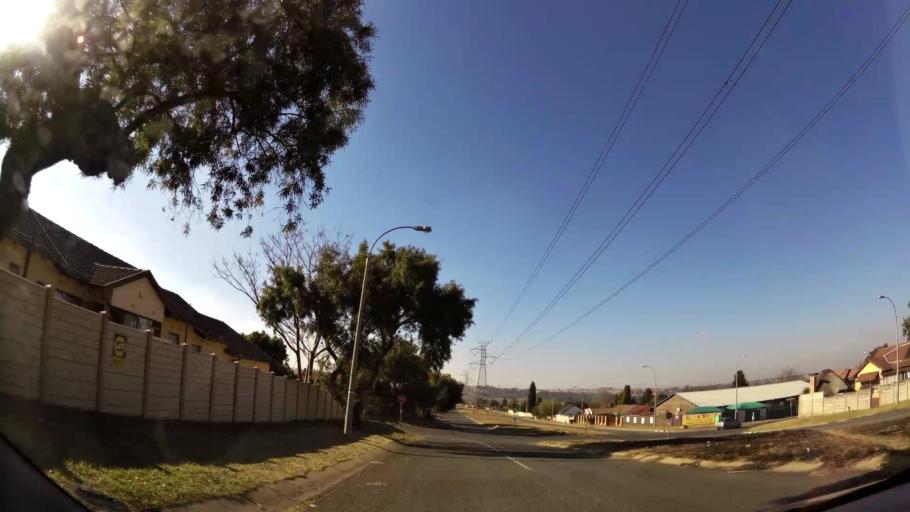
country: ZA
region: Gauteng
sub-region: City of Johannesburg Metropolitan Municipality
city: Roodepoort
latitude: -26.1622
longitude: 27.8242
